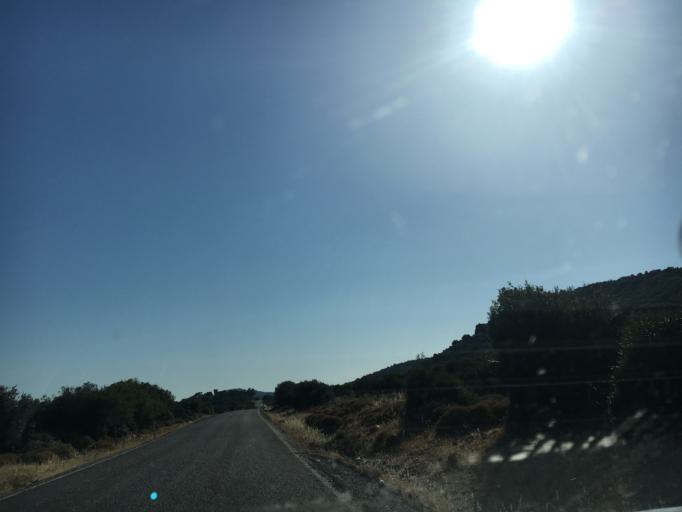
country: TR
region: Canakkale
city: Behram
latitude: 39.5073
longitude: 26.3755
